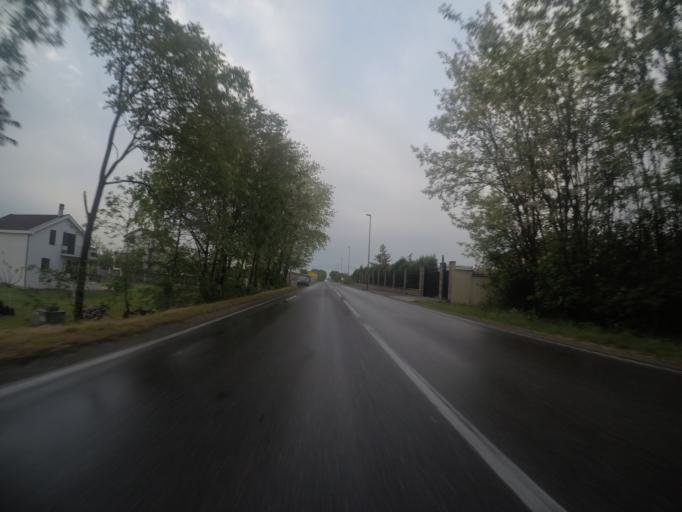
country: ME
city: Mojanovici
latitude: 42.3385
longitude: 19.2213
